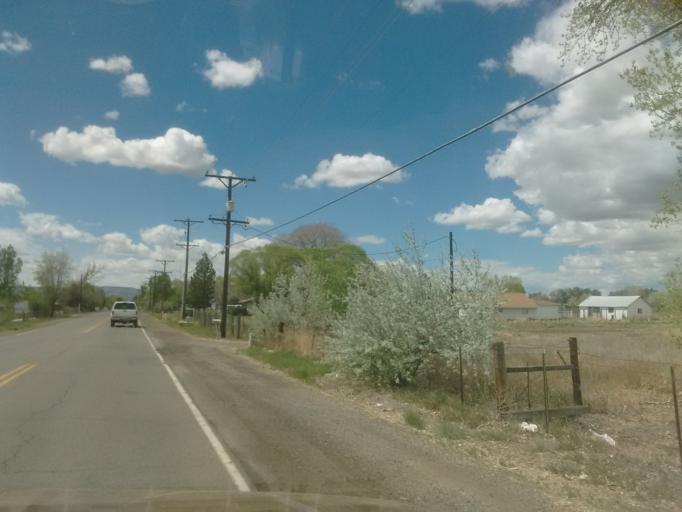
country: US
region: Colorado
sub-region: Mesa County
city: Fruitvale
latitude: 39.0774
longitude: -108.4726
